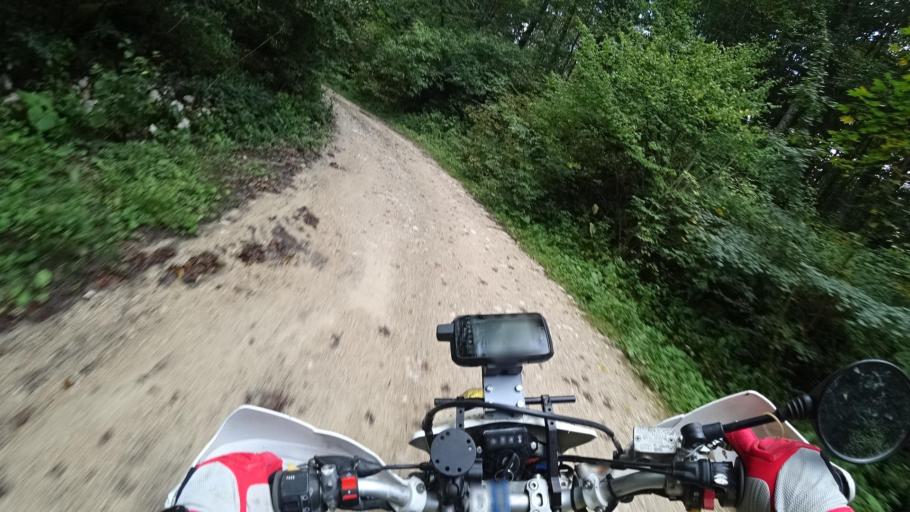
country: BA
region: Republika Srpska
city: Podbrdo
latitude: 44.5758
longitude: 17.0795
